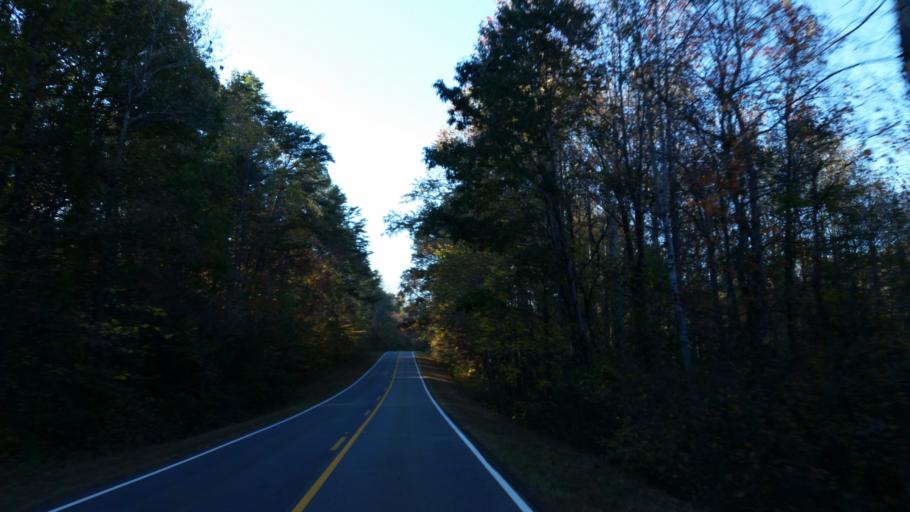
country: US
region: Georgia
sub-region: Pickens County
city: Jasper
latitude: 34.5257
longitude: -84.4745
